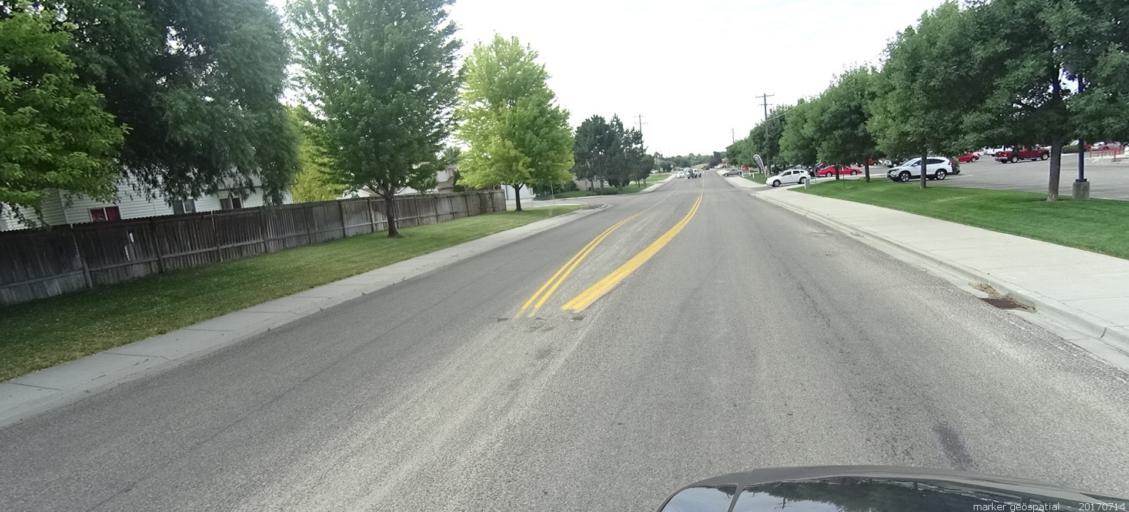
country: US
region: Idaho
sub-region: Ada County
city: Kuna
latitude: 43.4901
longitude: -116.4039
